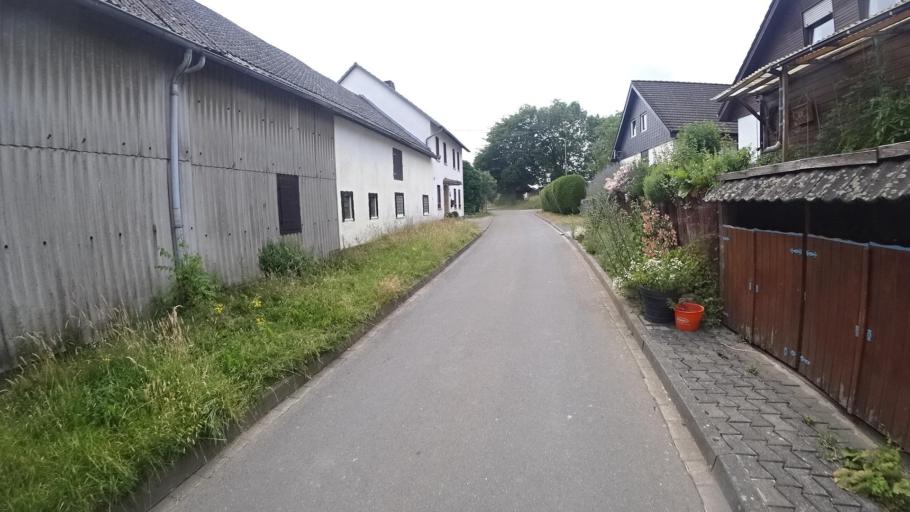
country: DE
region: Rheinland-Pfalz
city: Ziegenhain
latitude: 50.6782
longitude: 7.5285
